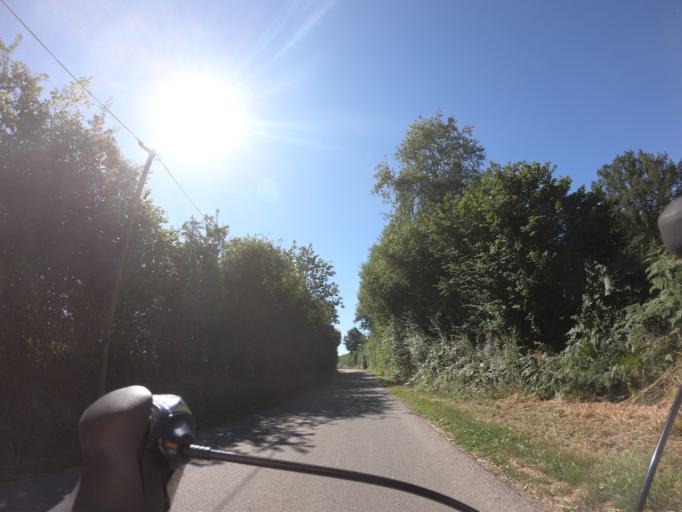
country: FR
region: Lower Normandy
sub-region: Departement de l'Orne
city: Saint-Denis-sur-Sarthon
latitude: 48.5179
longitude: -0.0833
